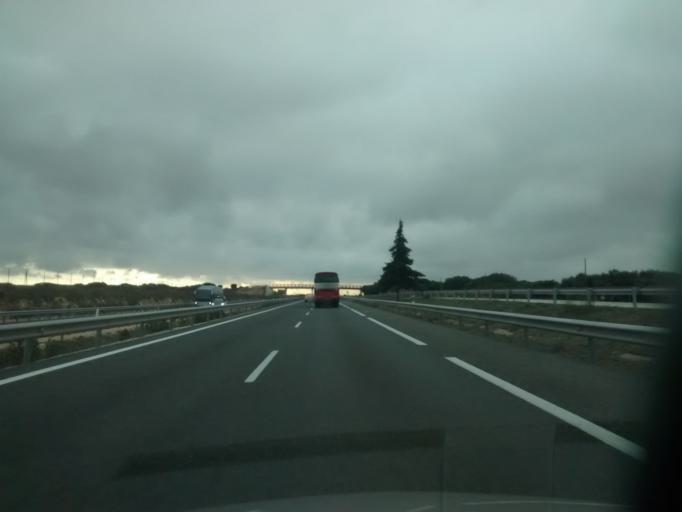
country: ES
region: Castille-La Mancha
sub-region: Provincia de Guadalajara
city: Utande
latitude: 40.8195
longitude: -2.9263
